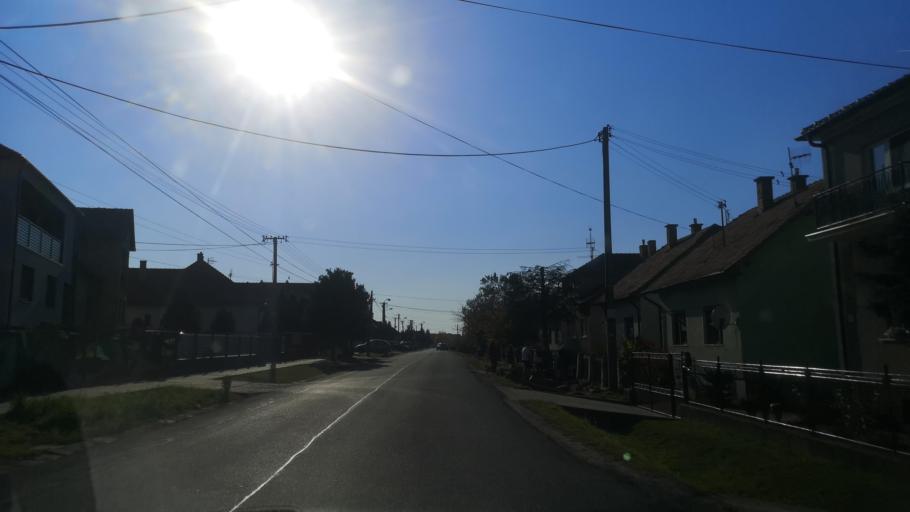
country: SK
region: Nitriansky
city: Zlate Moravce
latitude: 48.4201
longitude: 18.4191
